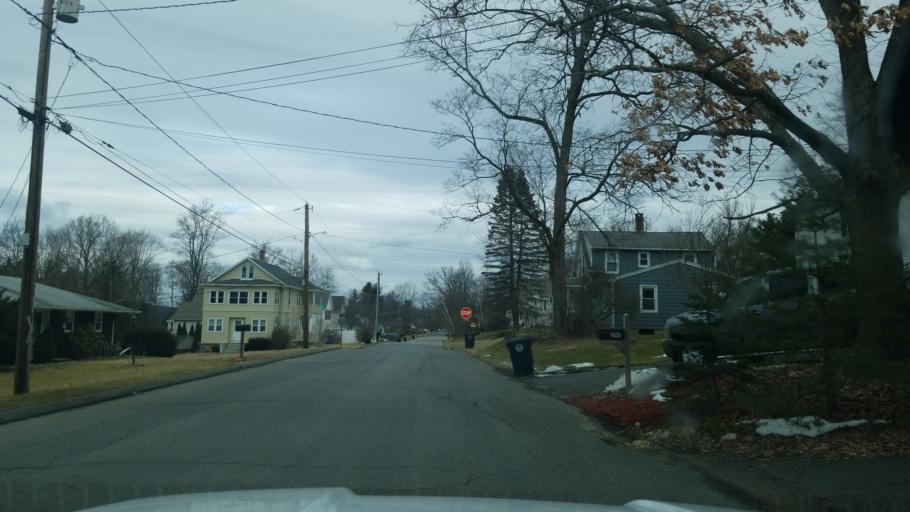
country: US
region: Connecticut
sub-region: Litchfield County
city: Torrington
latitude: 41.7980
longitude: -73.1048
